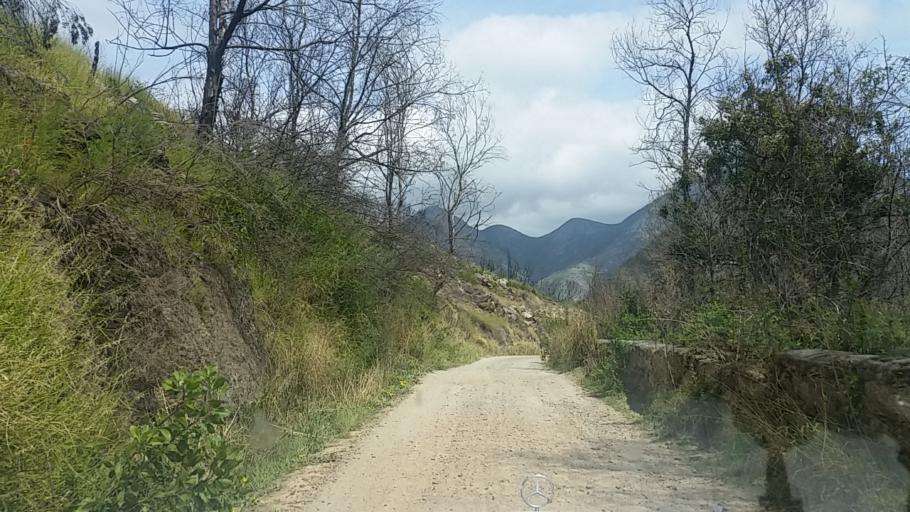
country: ZA
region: Western Cape
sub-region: Eden District Municipality
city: George
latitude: -33.8883
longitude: 22.4304
